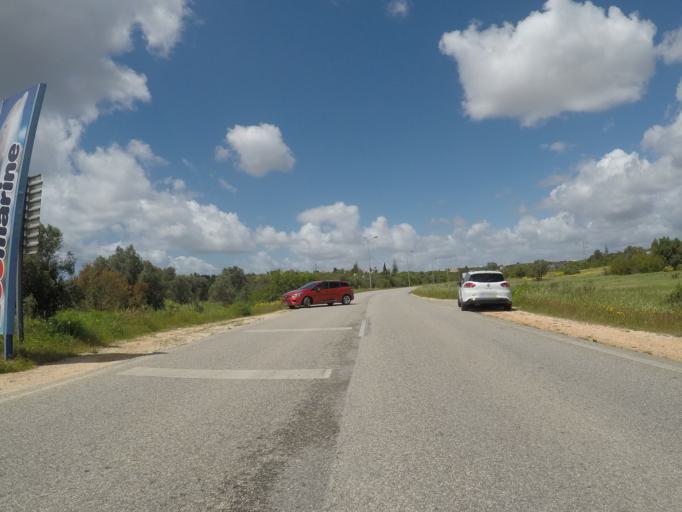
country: PT
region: Faro
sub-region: Silves
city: Armacao de Pera
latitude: 37.1162
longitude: -8.3464
